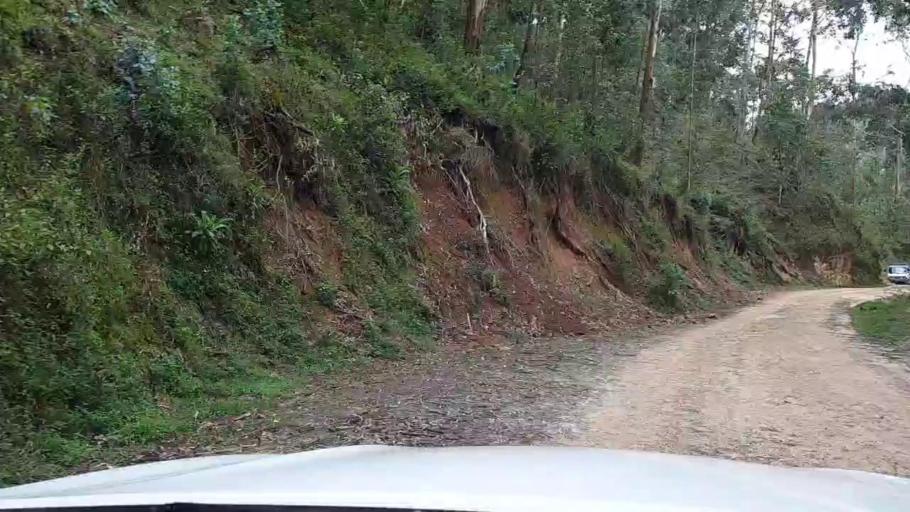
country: RW
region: Western Province
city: Kibuye
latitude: -2.2698
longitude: 29.3620
